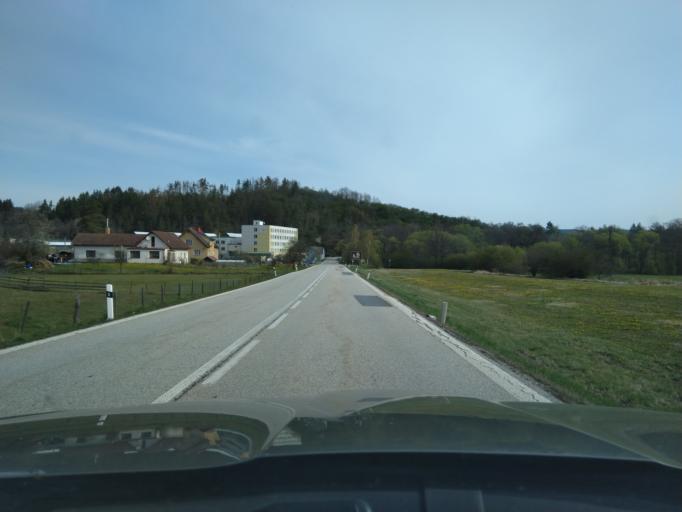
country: CZ
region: Jihocesky
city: Ckyne
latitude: 49.0968
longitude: 13.8020
